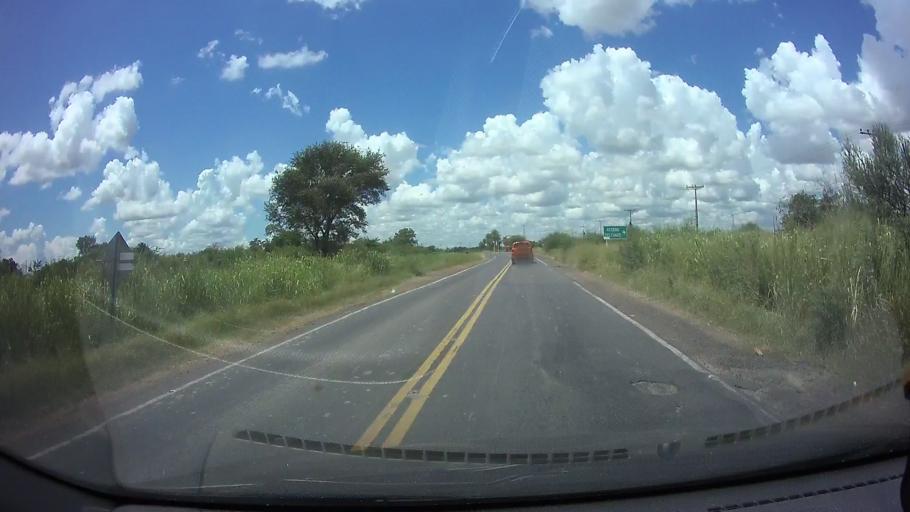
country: PY
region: Central
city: Colonia Mariano Roque Alonso
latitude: -25.1878
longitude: -57.5991
